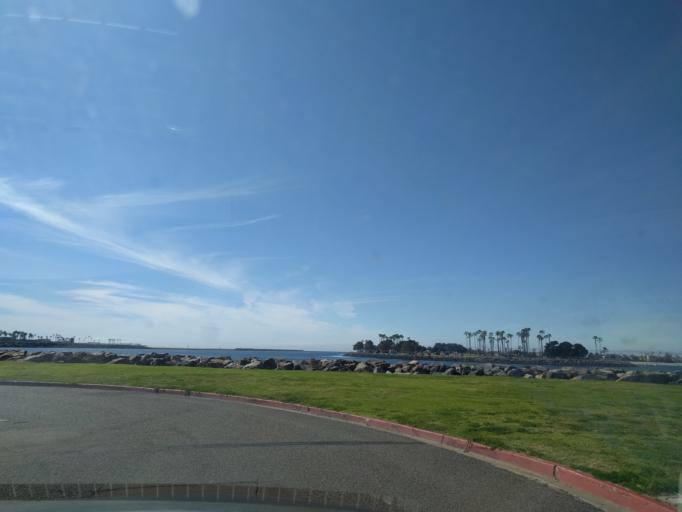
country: US
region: California
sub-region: San Diego County
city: La Jolla
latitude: 32.7611
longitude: -117.2412
